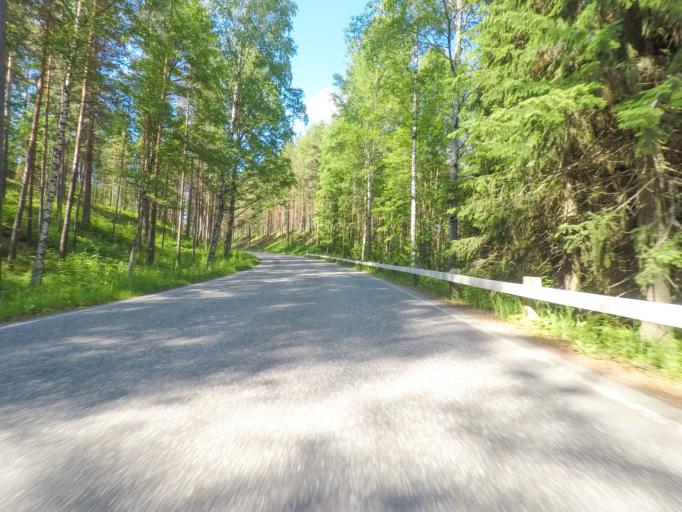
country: FI
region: Southern Savonia
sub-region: Savonlinna
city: Punkaharju
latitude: 61.8015
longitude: 29.3115
